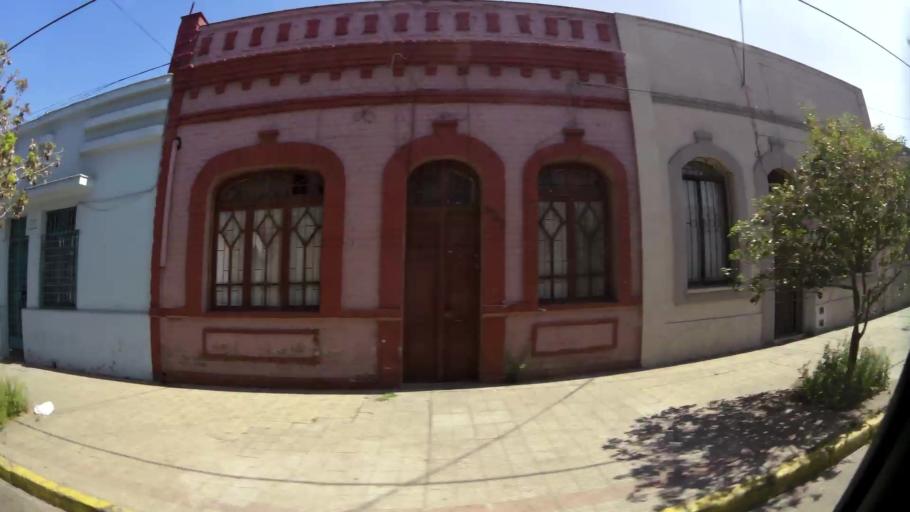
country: CL
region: Santiago Metropolitan
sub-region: Provincia de Santiago
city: Santiago
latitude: -33.4609
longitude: -70.6353
